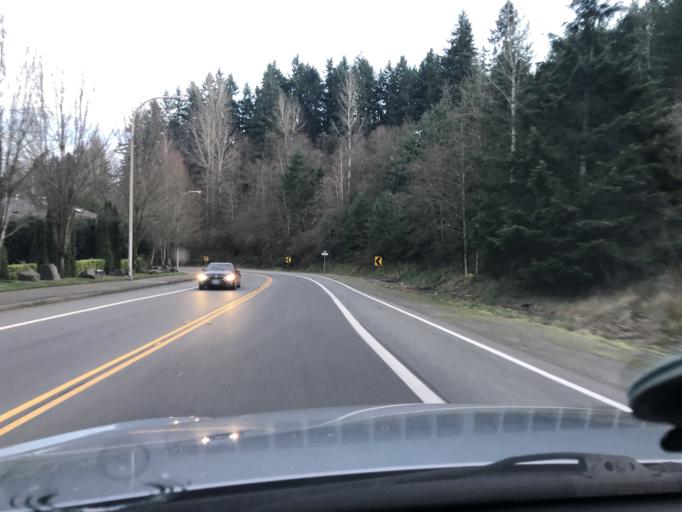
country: US
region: Washington
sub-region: King County
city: Lakeland North
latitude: 47.3166
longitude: -122.2583
